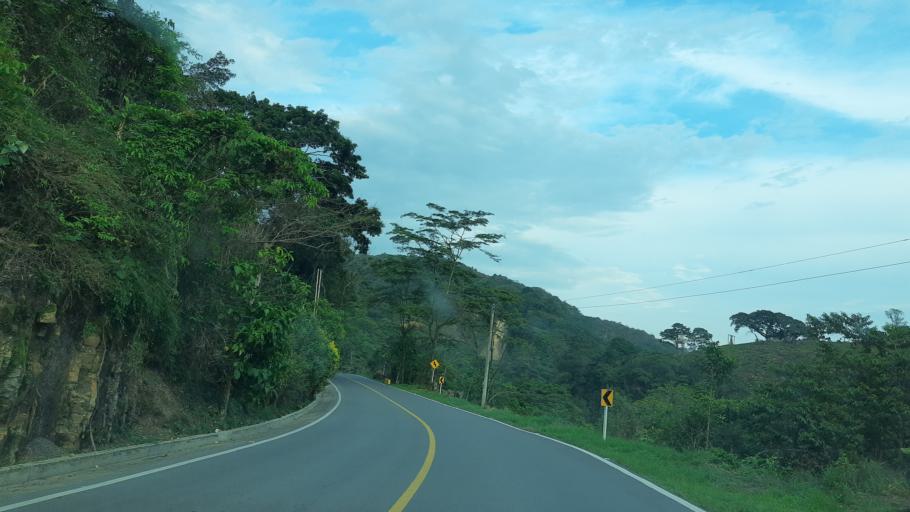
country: CO
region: Boyaca
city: San Luis de Gaceno
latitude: 4.8350
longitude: -73.2134
